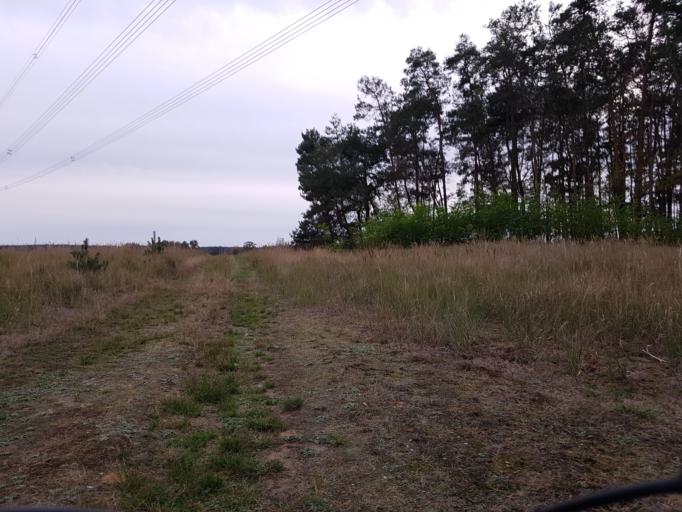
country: DE
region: Brandenburg
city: Schilda
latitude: 51.6185
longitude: 13.3689
